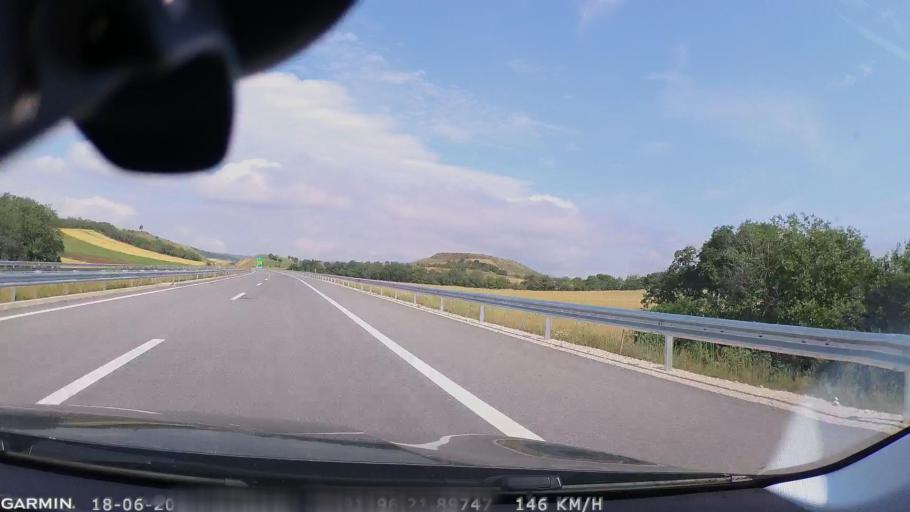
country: MK
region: Sveti Nikole
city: Gorobinci
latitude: 41.9121
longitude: 21.8959
